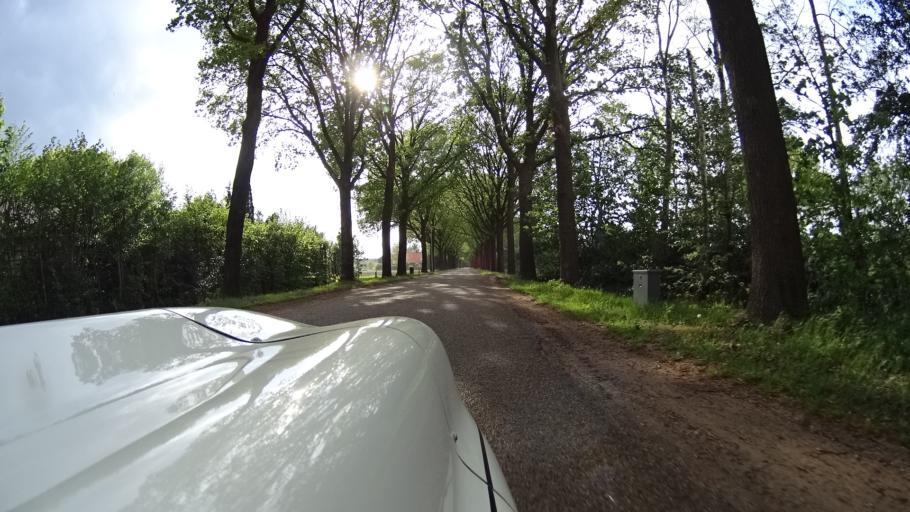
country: NL
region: North Brabant
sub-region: Gemeente Uden
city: Odiliapeel
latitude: 51.6361
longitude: 5.7183
